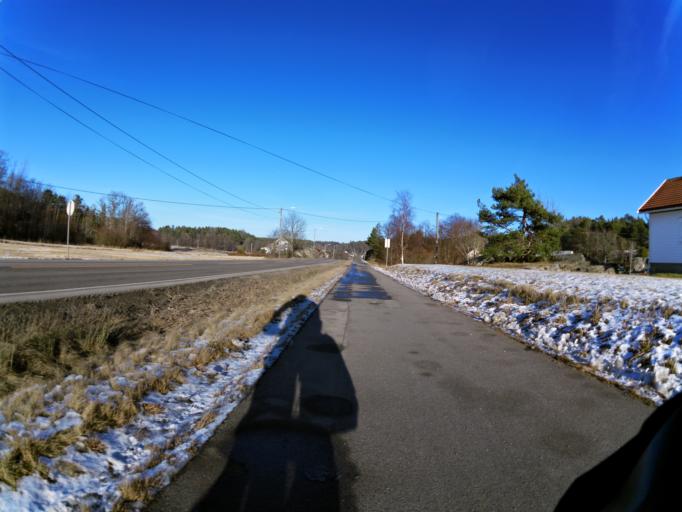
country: NO
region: Ostfold
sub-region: Fredrikstad
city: Fredrikstad
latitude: 59.1926
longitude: 10.8569
